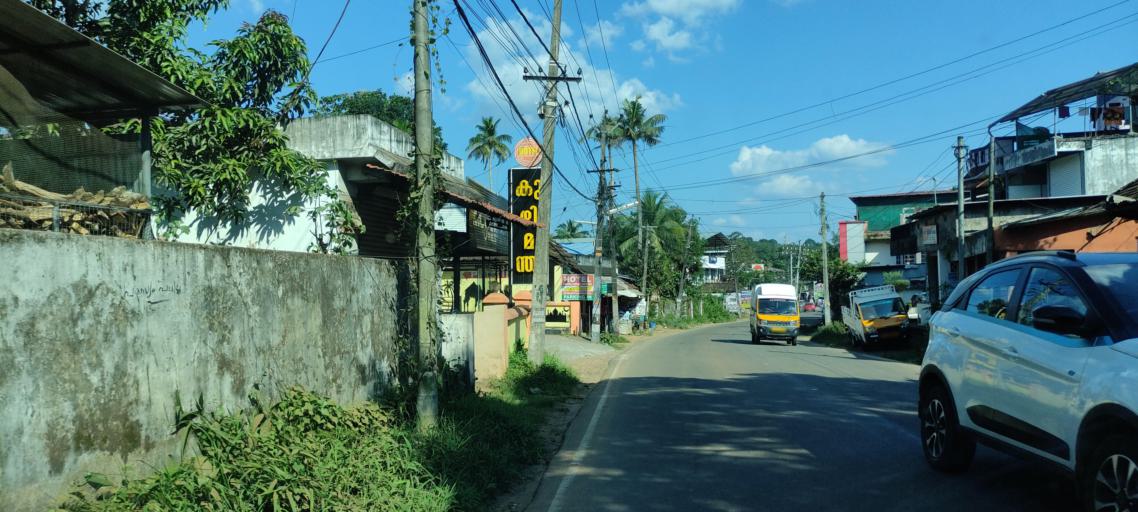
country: IN
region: Kerala
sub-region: Pattanamtitta
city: Pathanamthitta
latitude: 9.2682
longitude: 76.7968
